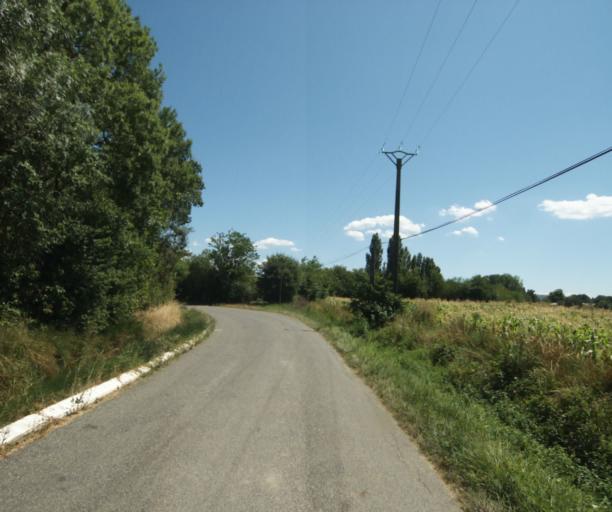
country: FR
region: Midi-Pyrenees
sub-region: Departement de la Haute-Garonne
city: Saint-Felix-Lauragais
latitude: 43.4588
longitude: 1.9441
